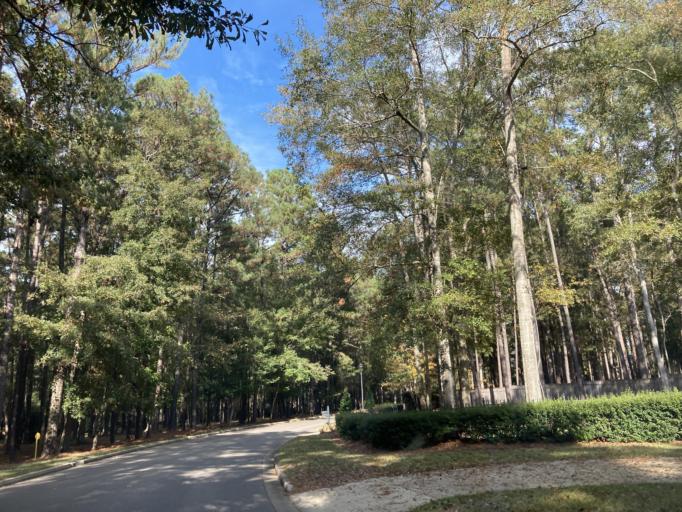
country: US
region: Mississippi
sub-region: Lamar County
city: West Hattiesburg
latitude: 31.3180
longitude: -89.4565
